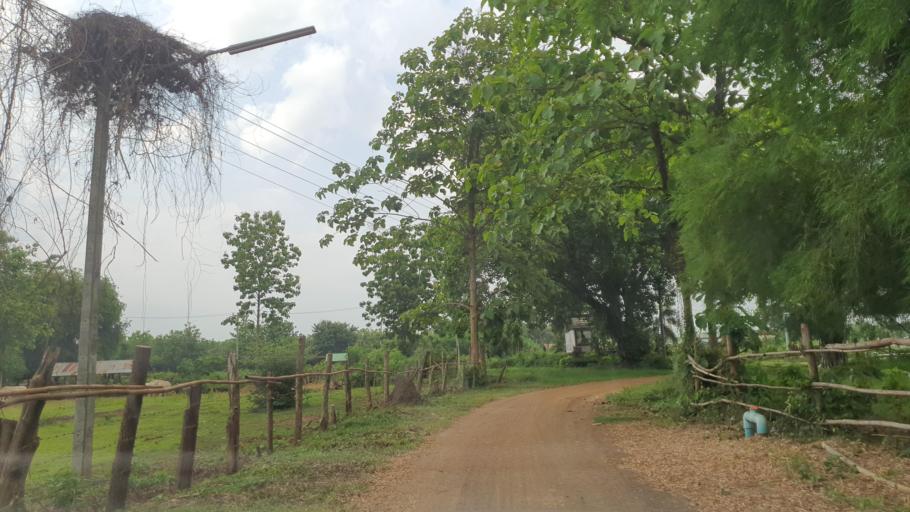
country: TH
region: Sukhothai
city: Thung Saliam
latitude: 17.2494
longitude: 99.5473
